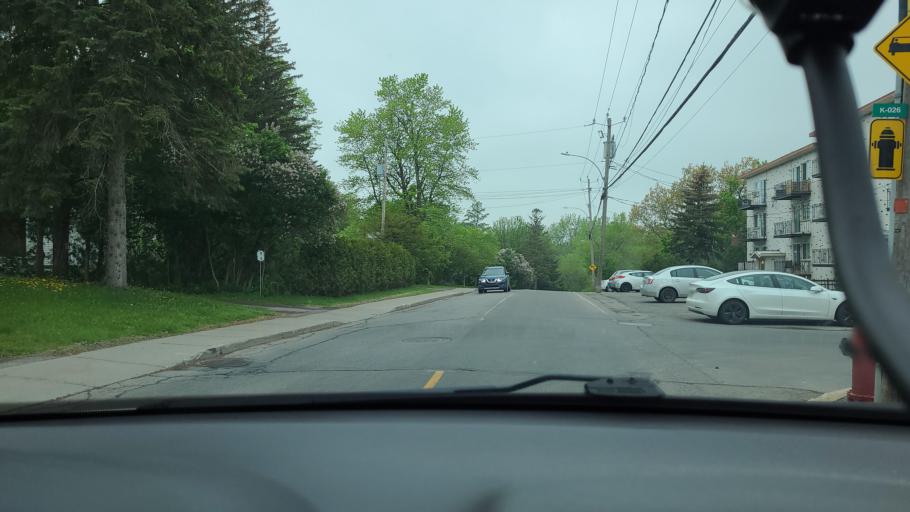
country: CA
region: Quebec
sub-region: Monteregie
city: L'Ile-Perrot
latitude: 45.3924
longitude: -73.9397
